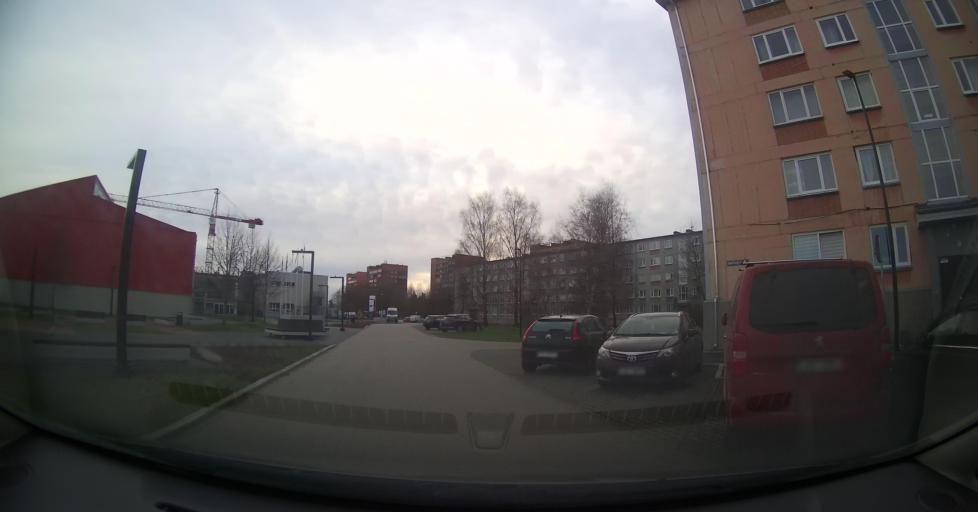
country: EE
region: Ida-Virumaa
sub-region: Johvi vald
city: Johvi
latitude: 59.3512
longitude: 27.4164
